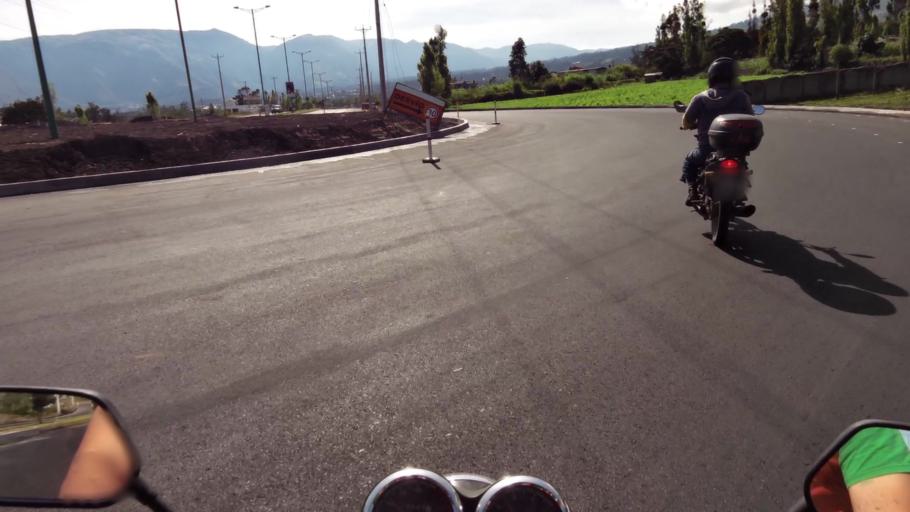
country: EC
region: Imbabura
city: Ibarra
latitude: 0.3331
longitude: -78.1562
